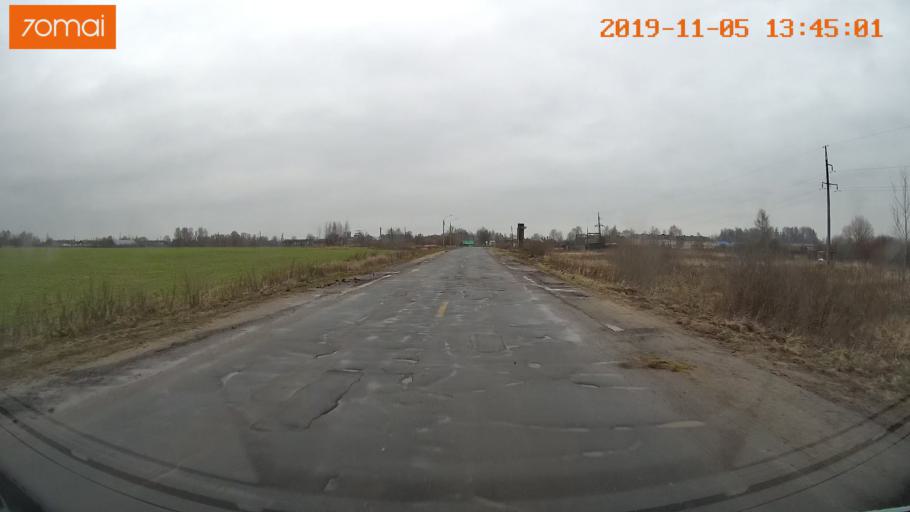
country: RU
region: Ivanovo
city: Shuya
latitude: 56.9853
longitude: 41.4119
